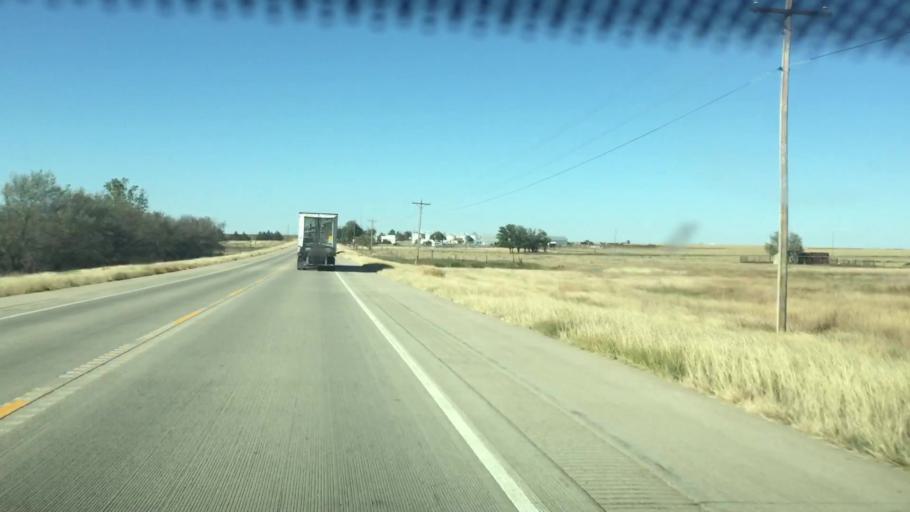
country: US
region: Colorado
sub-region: Kiowa County
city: Eads
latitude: 38.4592
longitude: -102.7306
